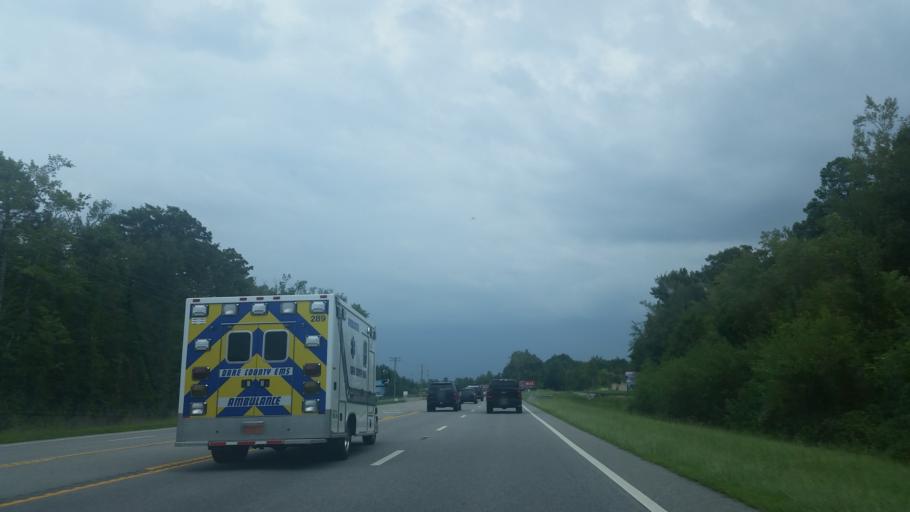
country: US
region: North Carolina
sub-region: Currituck County
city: Moyock
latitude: 36.4832
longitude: -76.1328
